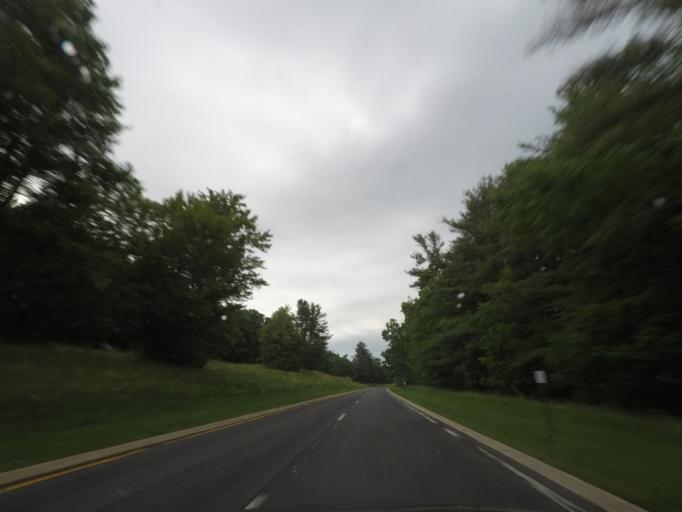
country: US
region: New York
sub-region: Columbia County
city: Chatham
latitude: 42.3008
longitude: -73.5820
